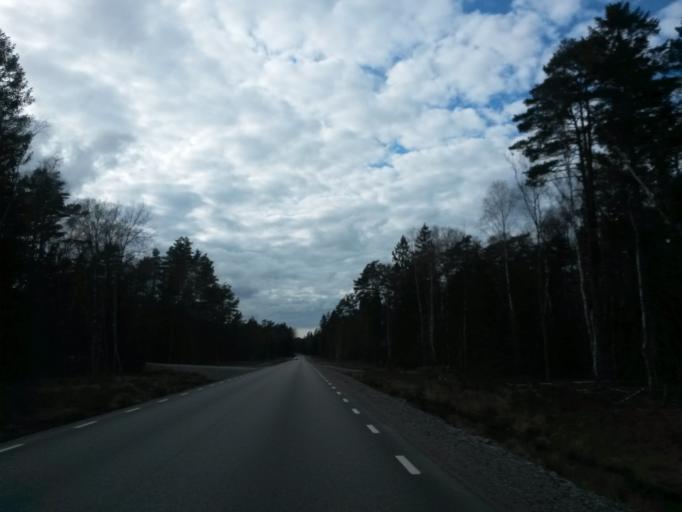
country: SE
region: Vaestra Goetaland
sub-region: Vargarda Kommun
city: Jonstorp
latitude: 57.9439
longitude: 12.6722
